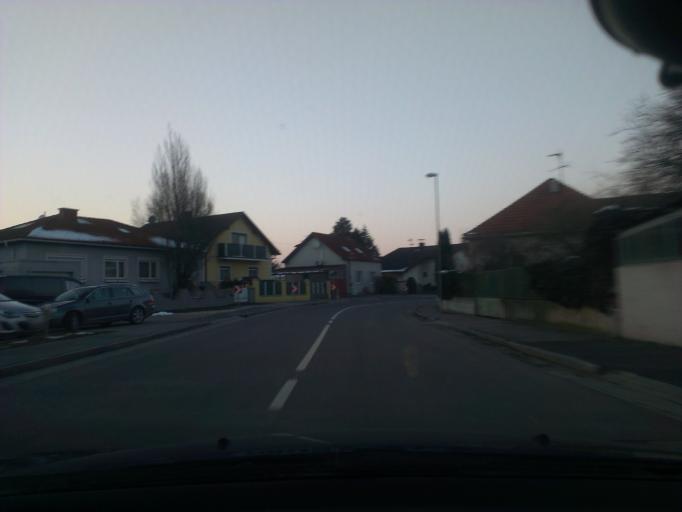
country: AT
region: Lower Austria
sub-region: Politischer Bezirk Bruck an der Leitha
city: Enzersdorf an der Fischa
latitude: 48.0883
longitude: 16.6090
